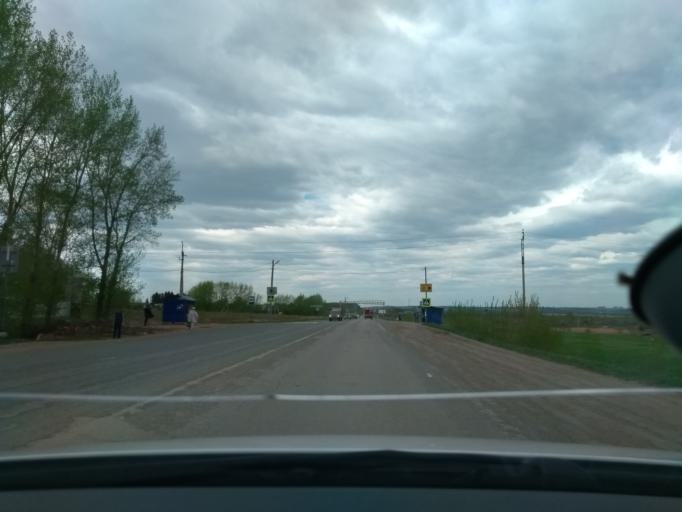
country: RU
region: Perm
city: Lobanovo
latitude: 57.8665
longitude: 56.2904
